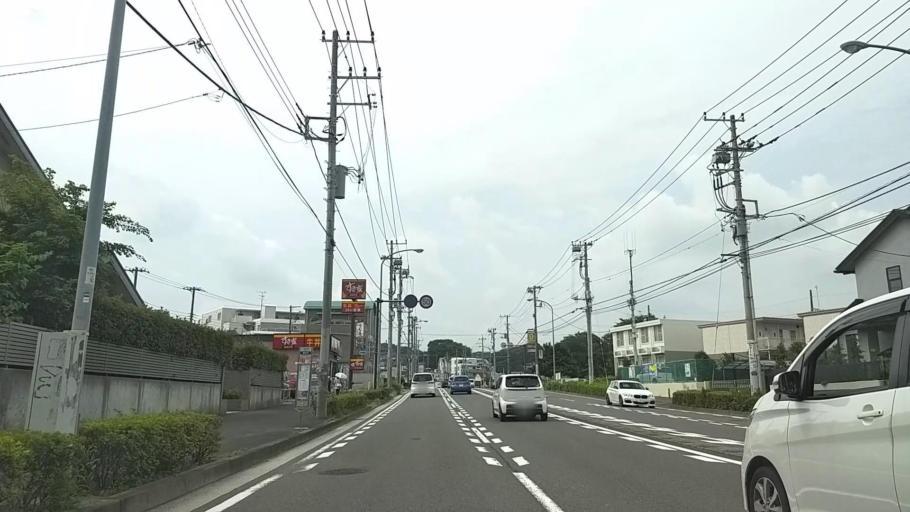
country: JP
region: Kanagawa
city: Minami-rinkan
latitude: 35.5093
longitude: 139.5447
